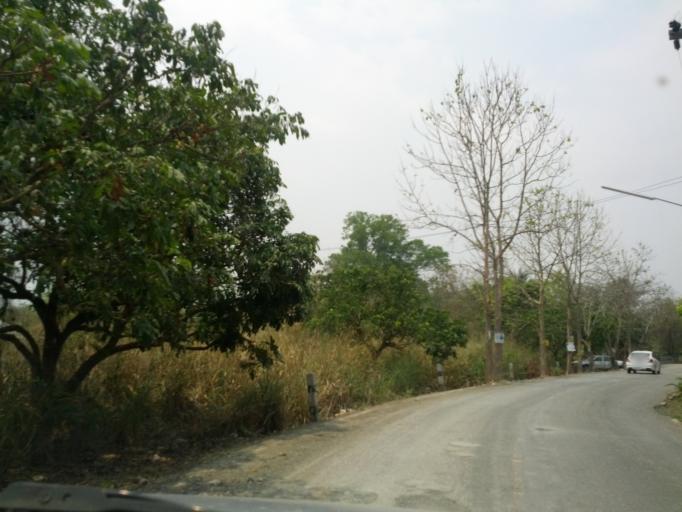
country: TH
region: Chiang Mai
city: San Sai
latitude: 18.9181
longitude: 99.0302
